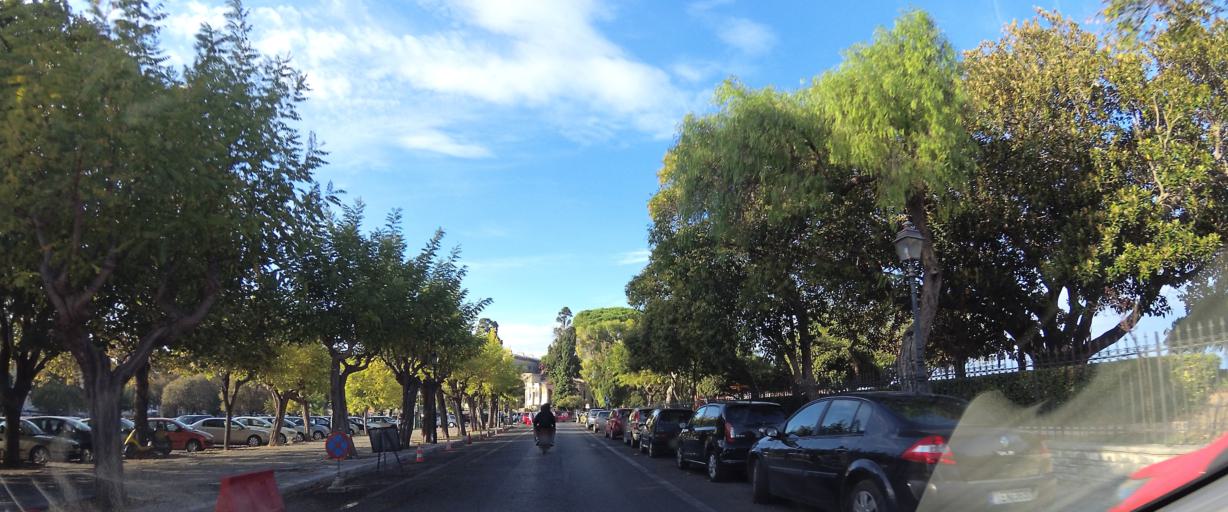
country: GR
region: Ionian Islands
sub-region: Nomos Kerkyras
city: Kerkyra
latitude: 39.6244
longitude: 19.9253
